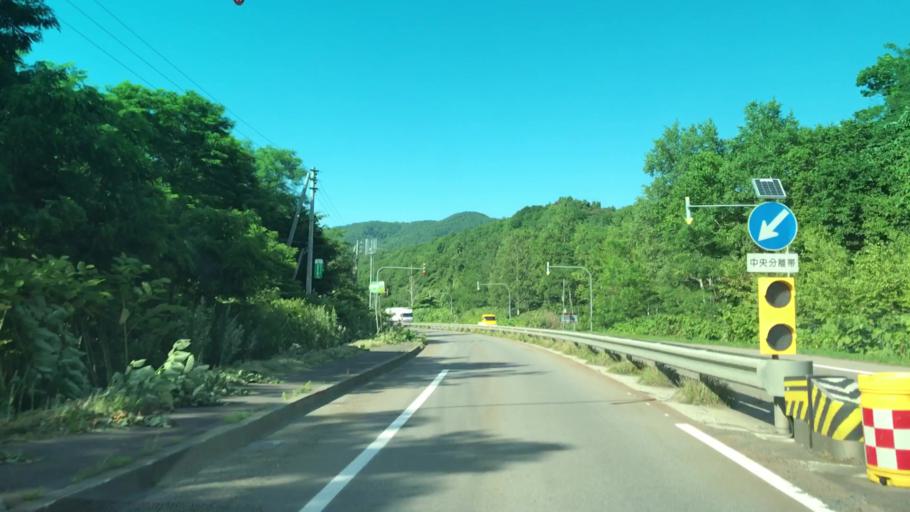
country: JP
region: Hokkaido
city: Iwanai
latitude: 42.9951
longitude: 140.6663
